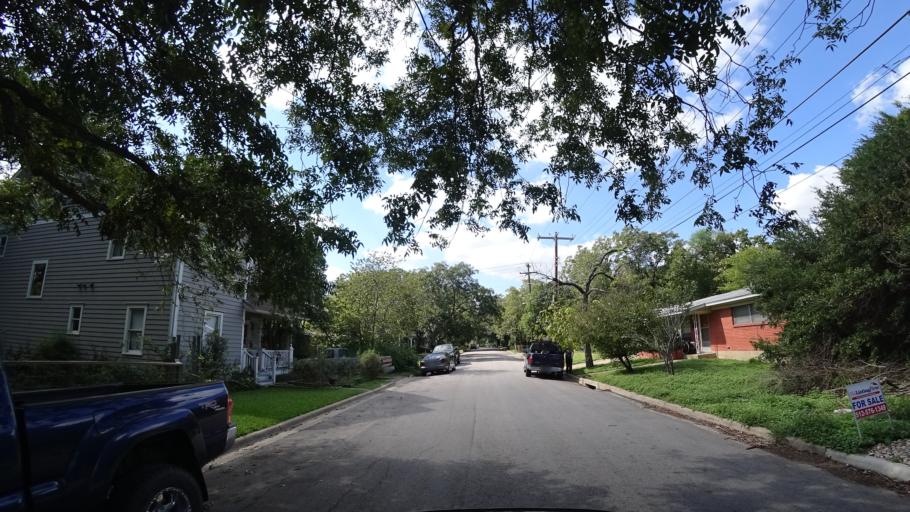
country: US
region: Texas
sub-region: Travis County
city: Austin
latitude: 30.3068
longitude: -97.7195
